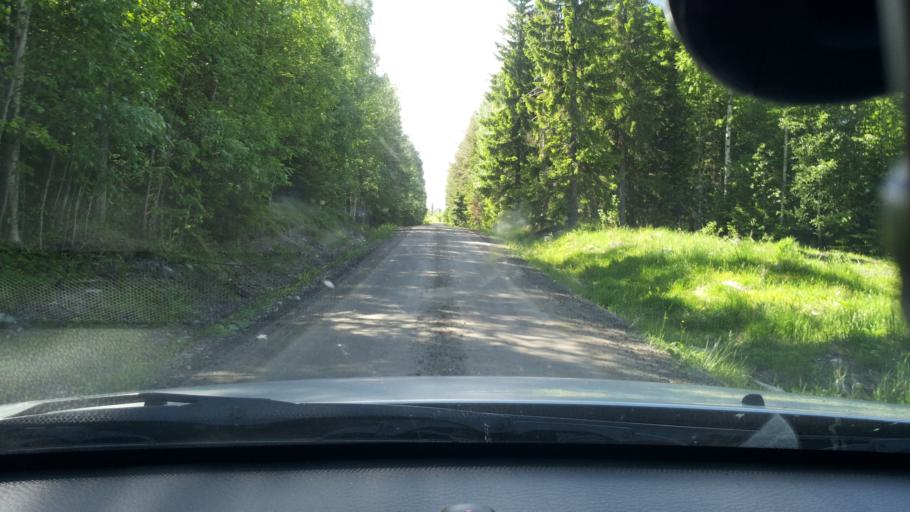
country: SE
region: Vaesternorrland
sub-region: Ange Kommun
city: Fransta
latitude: 62.3448
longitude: 16.3654
